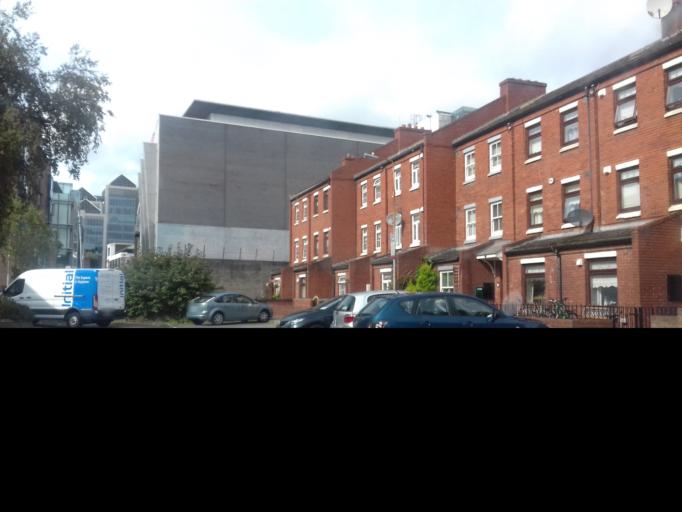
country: IE
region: Leinster
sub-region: Dublin City
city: Dublin
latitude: 53.3462
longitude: -6.2486
